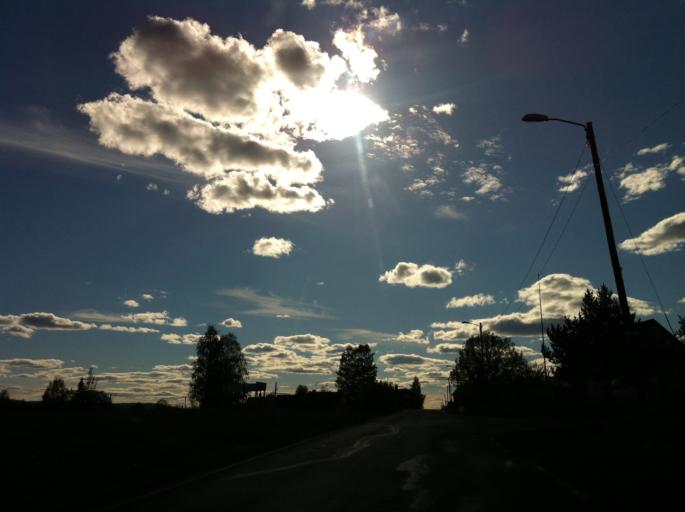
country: SE
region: Dalarna
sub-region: Leksand Municipality
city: Leksand
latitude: 60.7609
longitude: 14.9380
